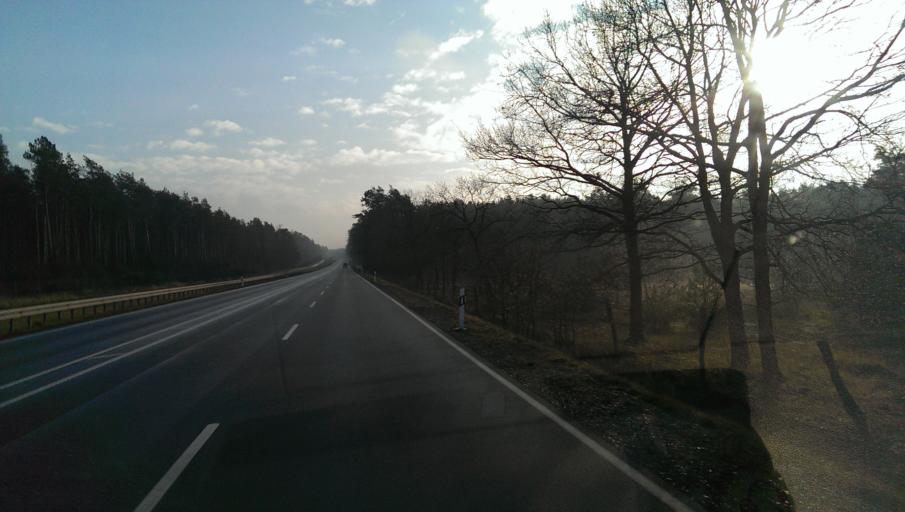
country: DE
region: Brandenburg
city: Herzberg
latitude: 51.6577
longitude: 13.2860
